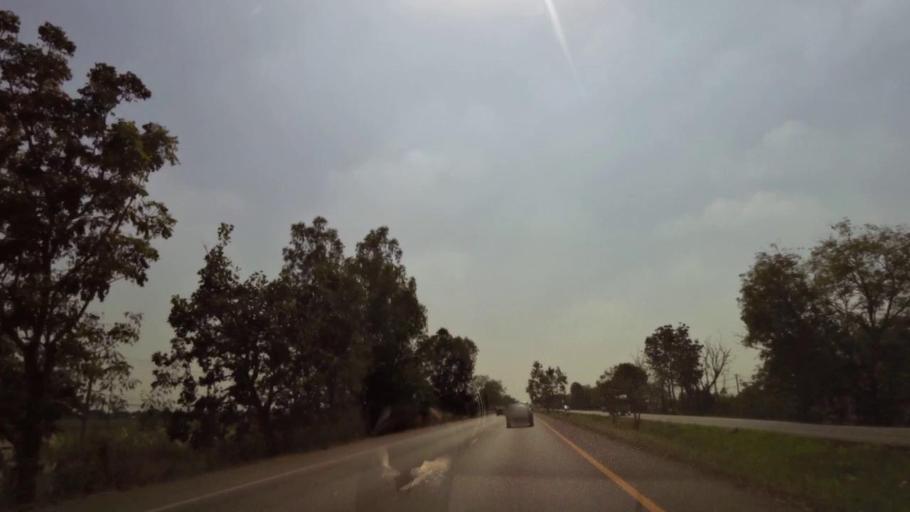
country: TH
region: Phichit
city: Wachira Barami
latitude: 16.4528
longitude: 100.1468
